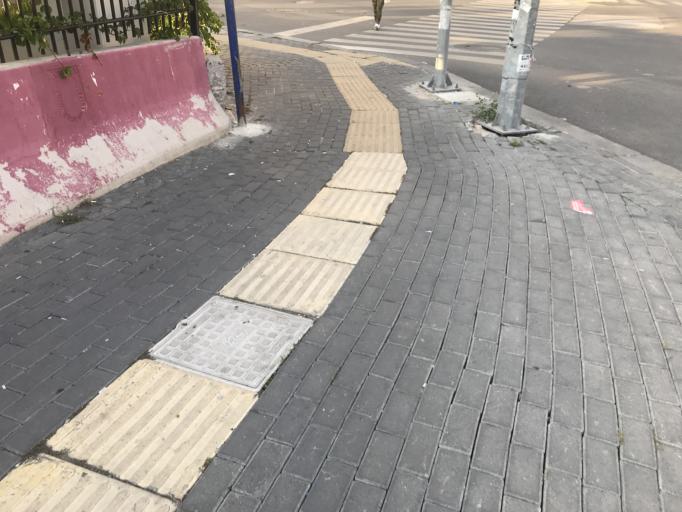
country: TR
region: Ankara
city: Ankara
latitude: 39.8726
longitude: 32.8323
